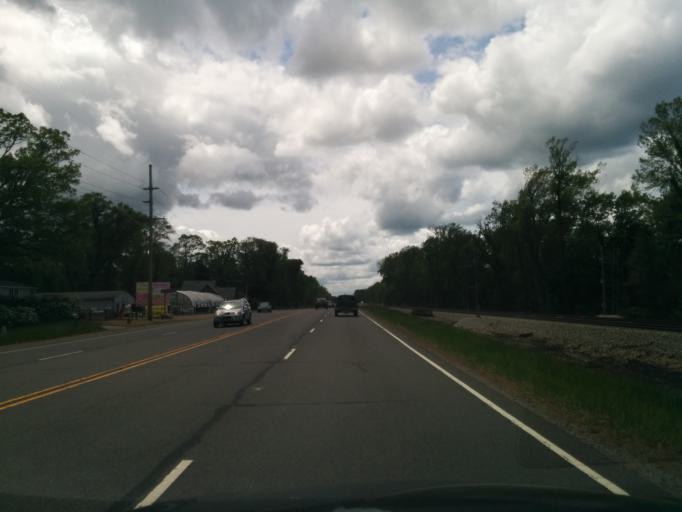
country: US
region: Indiana
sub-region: LaPorte County
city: Long Beach
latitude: 41.7330
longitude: -86.8573
